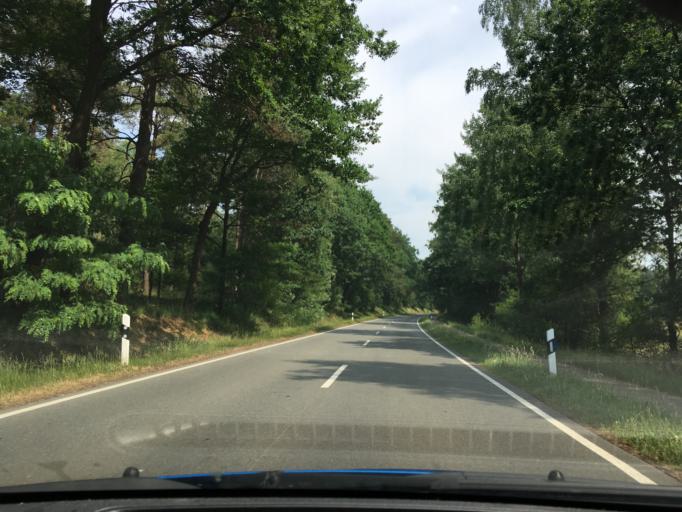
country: DE
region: Lower Saxony
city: Jesteburg
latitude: 53.2709
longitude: 9.9470
